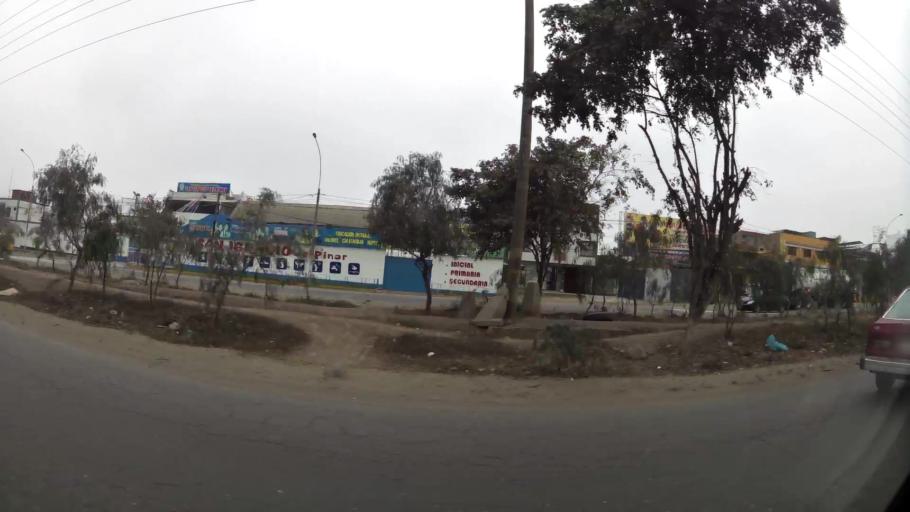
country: PE
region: Lima
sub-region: Lima
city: Urb. Santo Domingo
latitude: -11.9133
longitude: -77.0576
